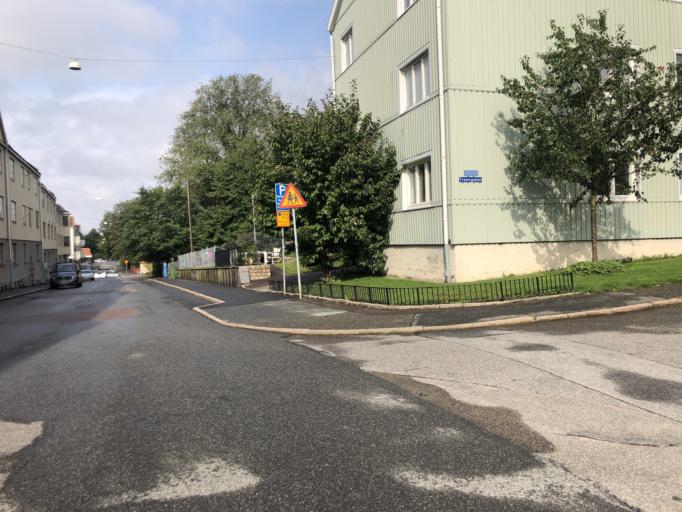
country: SE
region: Vaestra Goetaland
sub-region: Goteborg
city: Majorna
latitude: 57.6890
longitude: 11.9167
